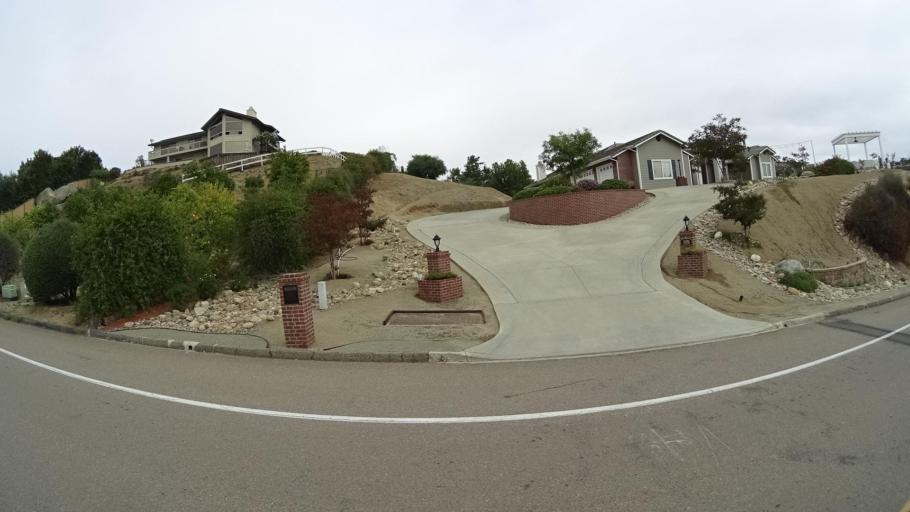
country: US
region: California
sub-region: San Diego County
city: Granite Hills
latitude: 32.7723
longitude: -116.9140
